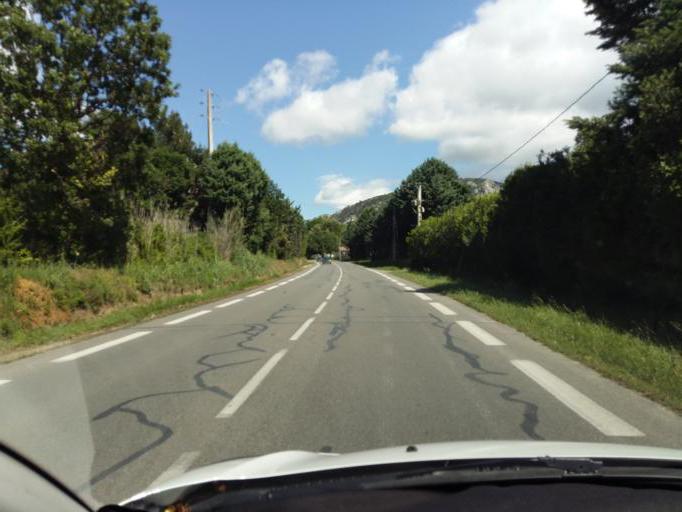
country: FR
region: Provence-Alpes-Cote d'Azur
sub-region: Departement du Vaucluse
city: Taillades
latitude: 43.8447
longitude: 5.0909
